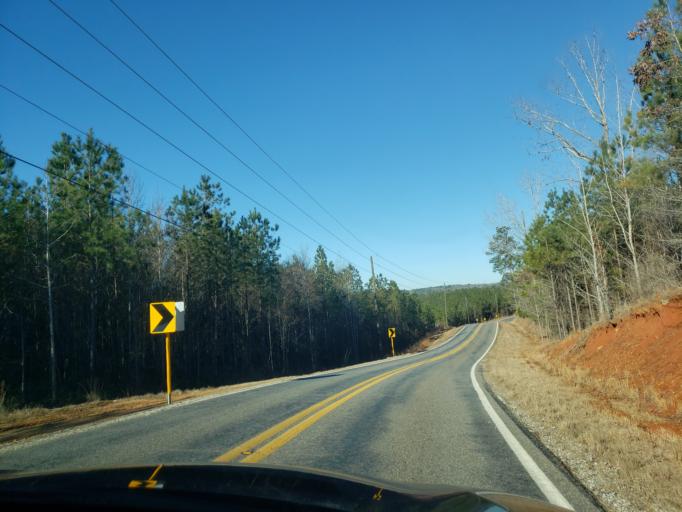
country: US
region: Alabama
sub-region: Elmore County
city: Tallassee
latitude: 32.6708
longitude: -85.8882
